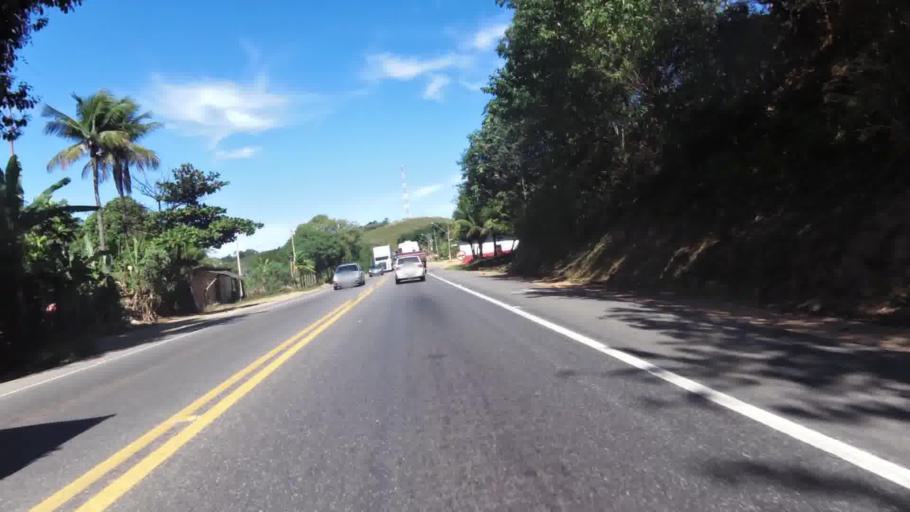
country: BR
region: Espirito Santo
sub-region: Iconha
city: Iconha
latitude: -20.8367
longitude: -40.8678
